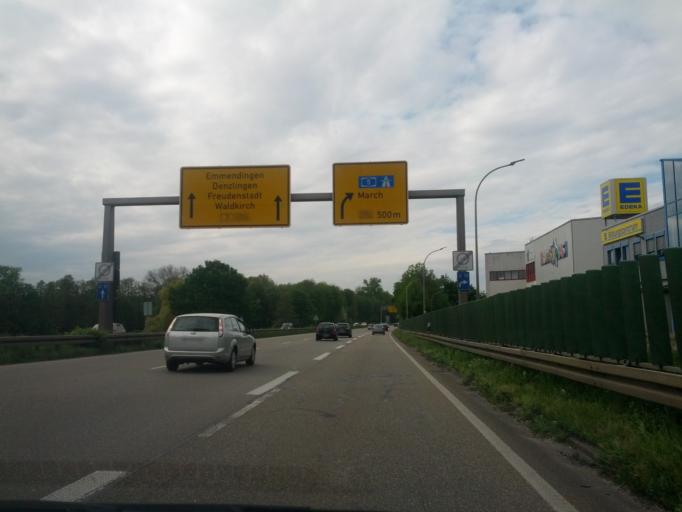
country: DE
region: Baden-Wuerttemberg
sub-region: Freiburg Region
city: Gundelfingen
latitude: 48.0393
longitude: 7.8593
